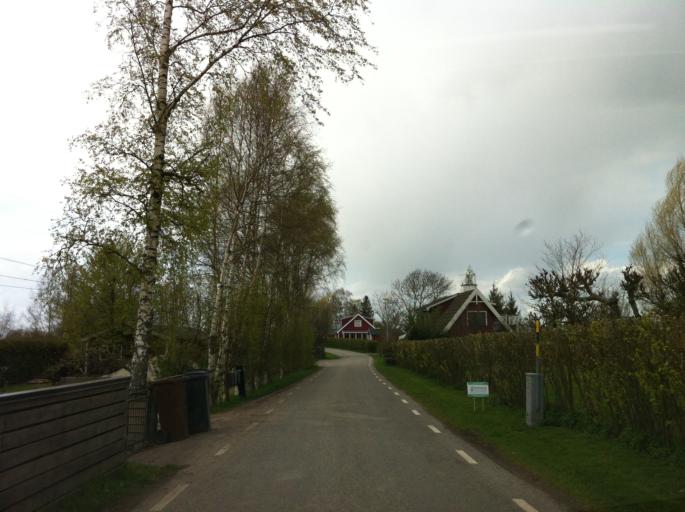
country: SE
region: Skane
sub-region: Svalovs Kommun
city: Teckomatorp
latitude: 55.8548
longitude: 13.0627
